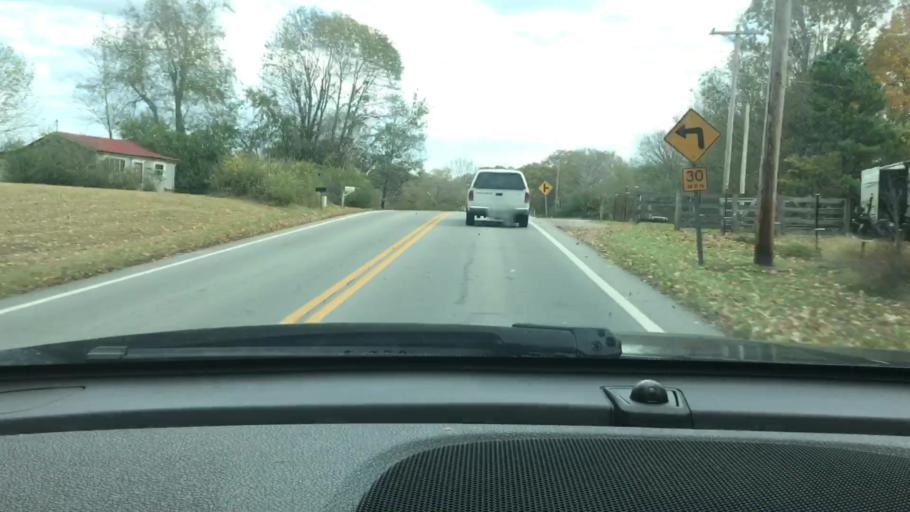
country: US
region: Tennessee
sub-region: Dickson County
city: Charlotte
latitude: 36.2115
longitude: -87.2628
